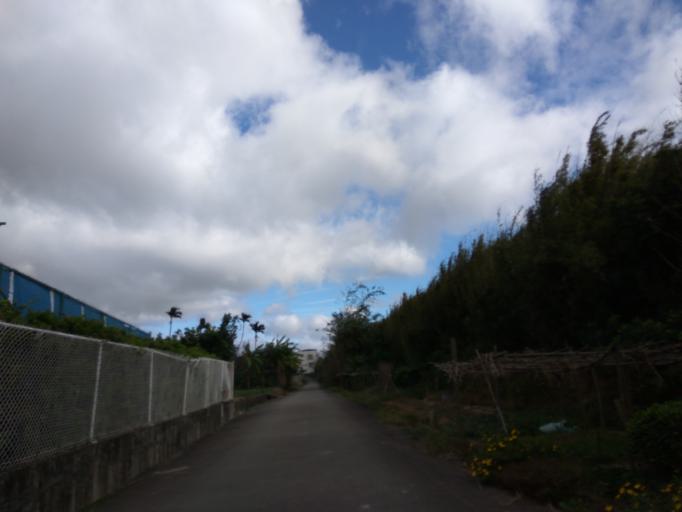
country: TW
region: Taiwan
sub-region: Hsinchu
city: Zhubei
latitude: 24.9709
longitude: 121.0950
